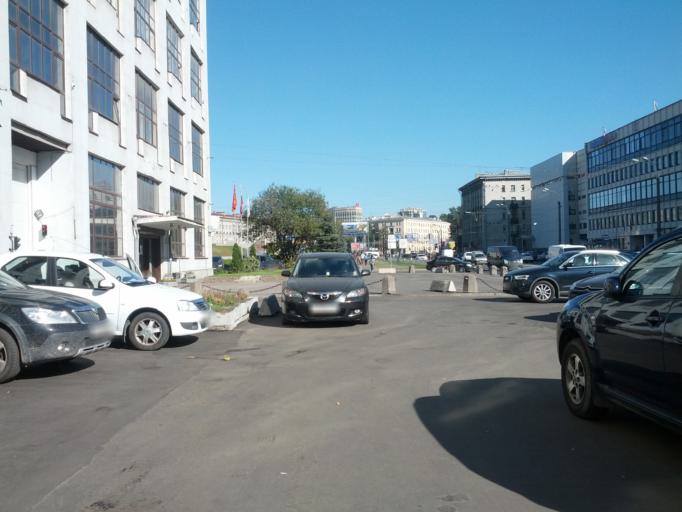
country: RU
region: Leningrad
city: Sampsonievskiy
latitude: 59.9826
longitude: 30.3304
